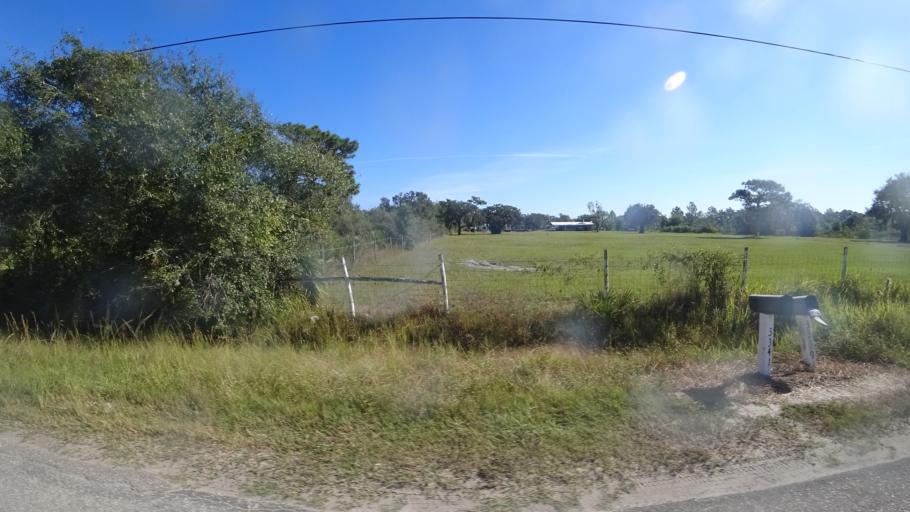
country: US
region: Florida
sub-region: Hillsborough County
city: Sun City Center
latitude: 27.6531
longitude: -82.3563
